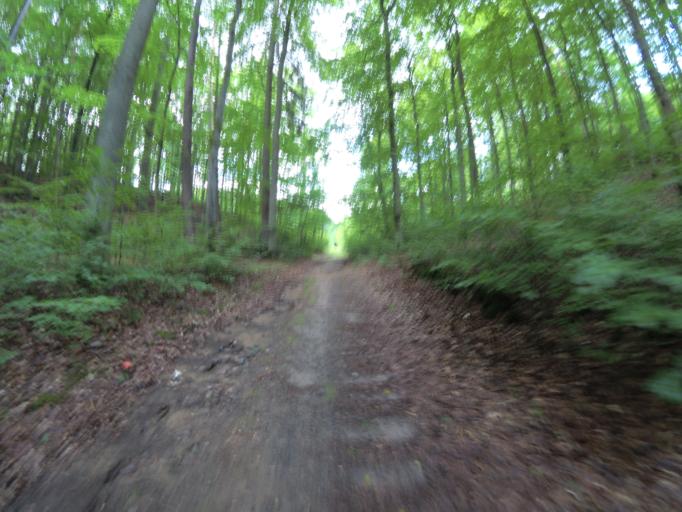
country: PL
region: Pomeranian Voivodeship
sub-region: Gdynia
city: Wielki Kack
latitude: 54.5072
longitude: 18.4410
